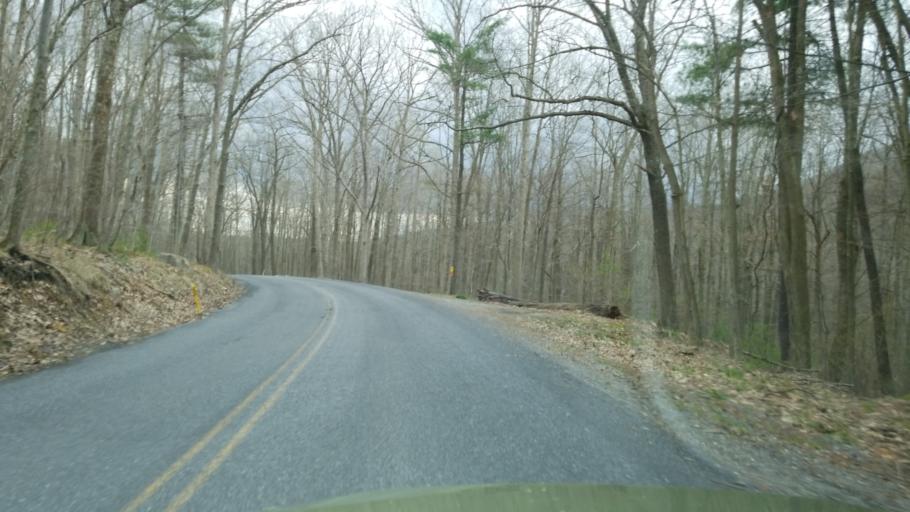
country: US
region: Pennsylvania
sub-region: Blair County
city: Tipton
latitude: 40.6887
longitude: -78.3316
